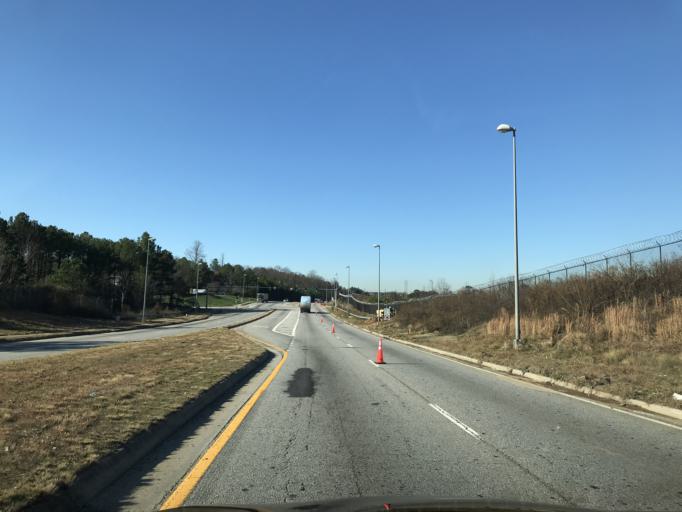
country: US
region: Georgia
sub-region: Fulton County
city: College Park
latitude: 33.6185
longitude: -84.4236
